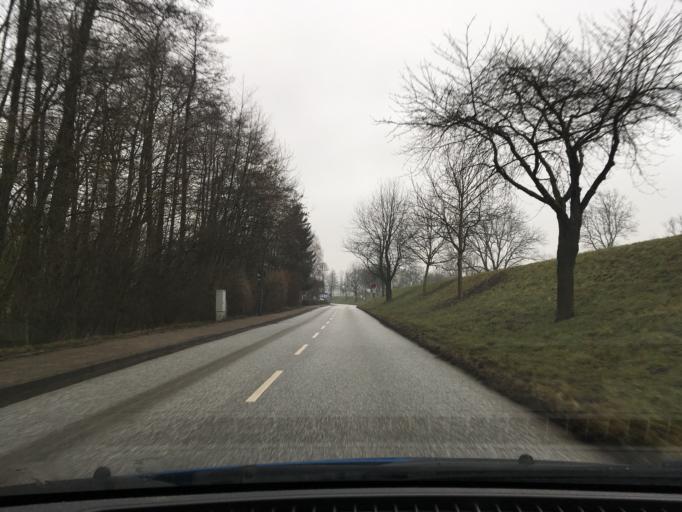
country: DE
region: Hamburg
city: Altona
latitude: 53.5058
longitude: 9.8763
